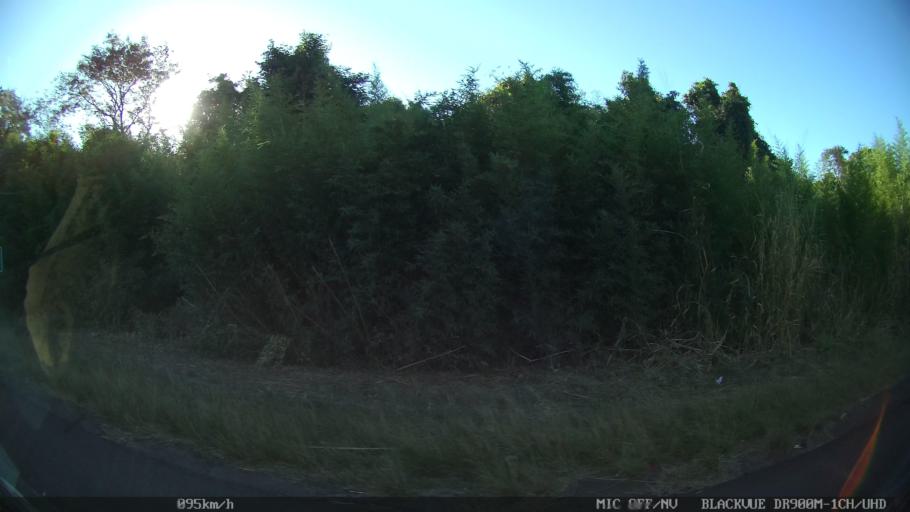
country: BR
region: Sao Paulo
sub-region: Guapiacu
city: Guapiacu
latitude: -20.7574
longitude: -49.1631
